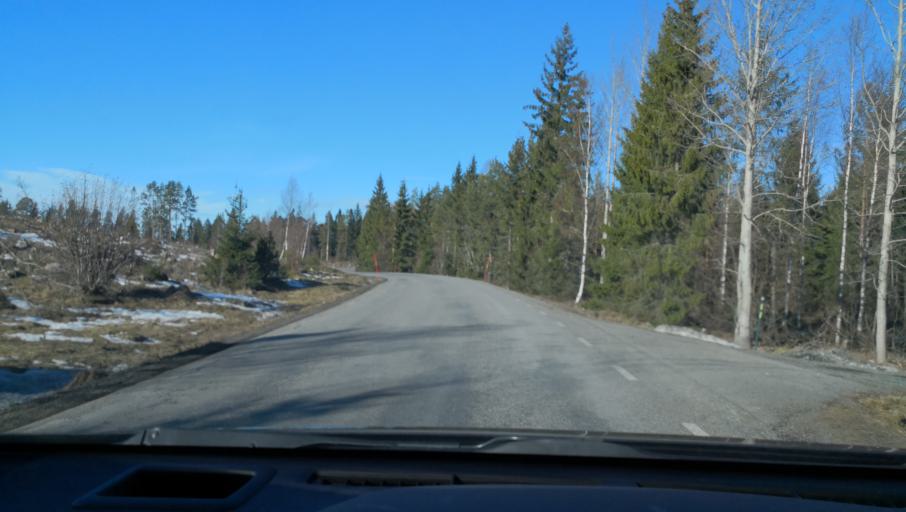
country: SE
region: Uppsala
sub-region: Osthammars Kommun
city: Osterbybruk
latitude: 60.2296
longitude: 17.9196
